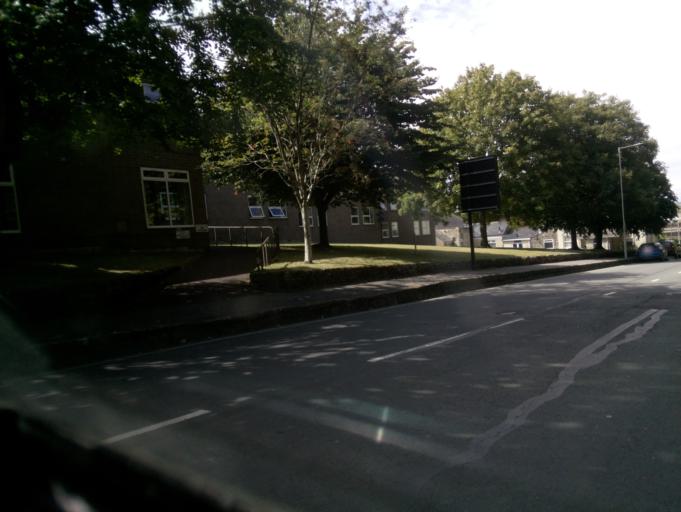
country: GB
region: England
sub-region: Dorset
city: Dorchester
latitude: 50.7157
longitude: -2.4417
